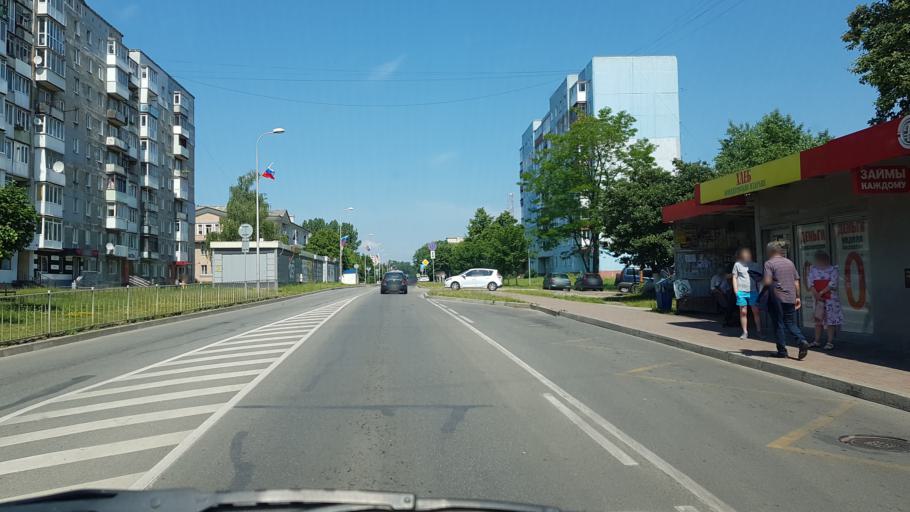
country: RU
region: Kaliningrad
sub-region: Gorod Kaliningrad
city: Baltiysk
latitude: 54.6553
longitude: 19.9121
